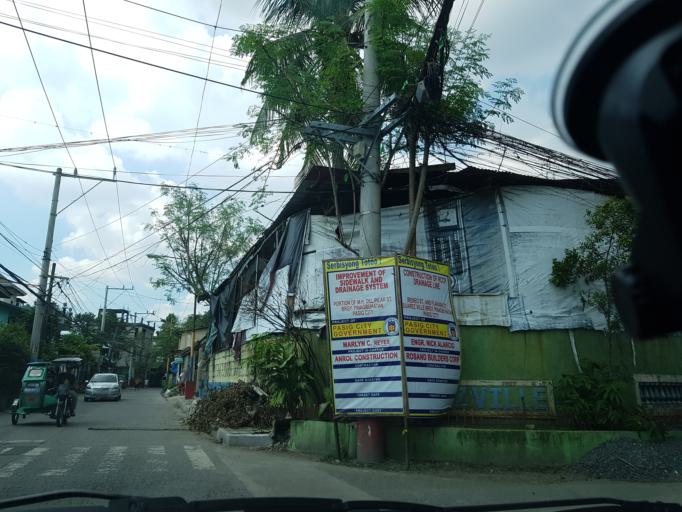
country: PH
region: Calabarzon
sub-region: Province of Rizal
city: Pateros
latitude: 14.5605
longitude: 121.0894
